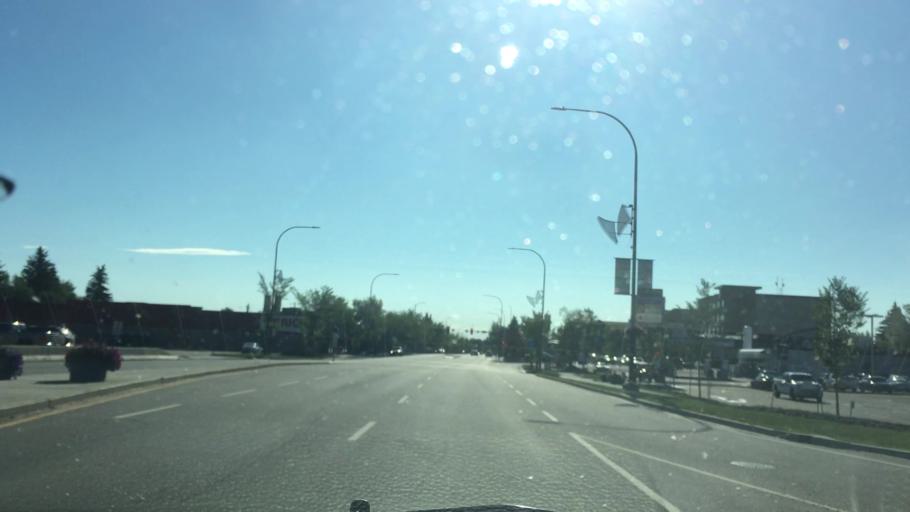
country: CA
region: Alberta
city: Leduc
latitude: 53.2647
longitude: -113.5613
